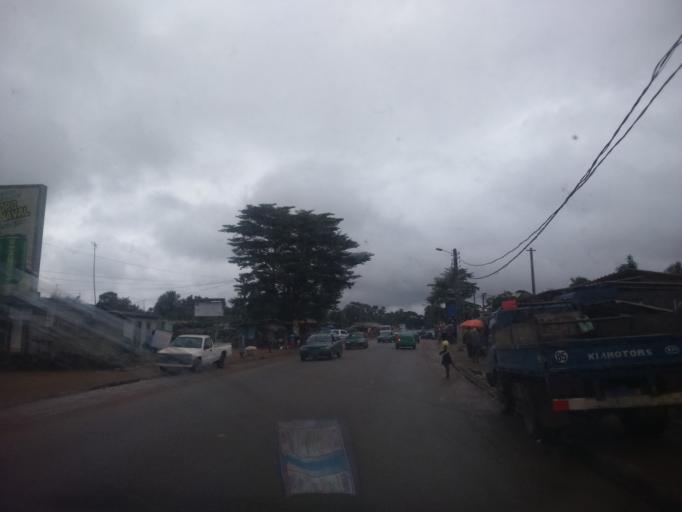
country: CI
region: Sud-Comoe
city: Bonoua
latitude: 5.2724
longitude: -3.5934
